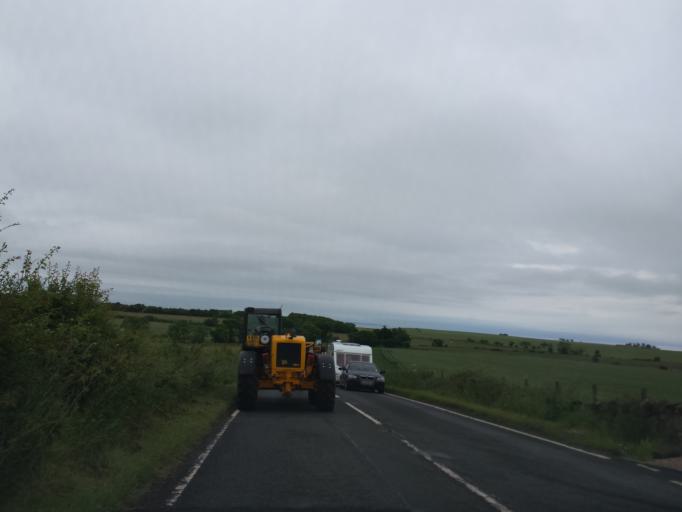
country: GB
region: Scotland
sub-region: Fife
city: Saint Andrews
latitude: 56.3032
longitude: -2.8278
